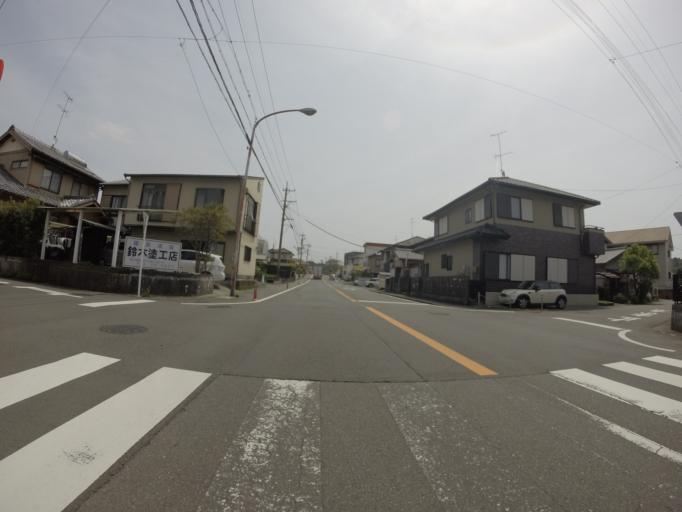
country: JP
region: Shizuoka
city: Kakegawa
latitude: 34.7679
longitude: 138.0261
